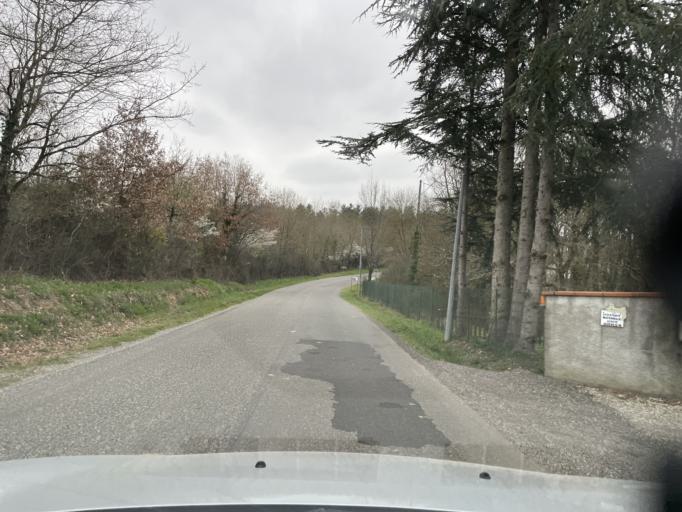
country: FR
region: Midi-Pyrenees
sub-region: Departement du Gers
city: Pujaudran
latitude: 43.5966
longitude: 1.1507
